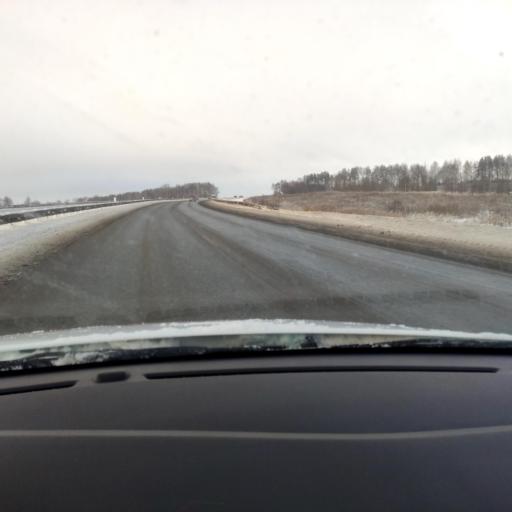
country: RU
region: Tatarstan
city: Vysokaya Gora
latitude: 55.7605
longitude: 49.3634
